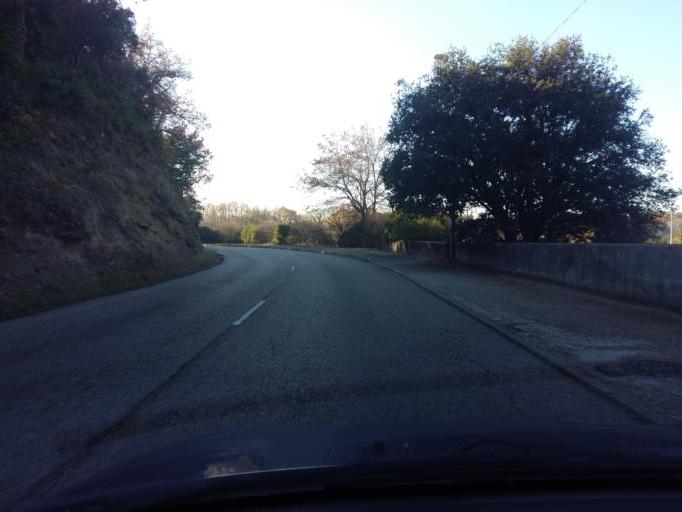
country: FR
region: Rhone-Alpes
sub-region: Departement de la Drome
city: Grignan
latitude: 44.4160
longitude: 4.9081
